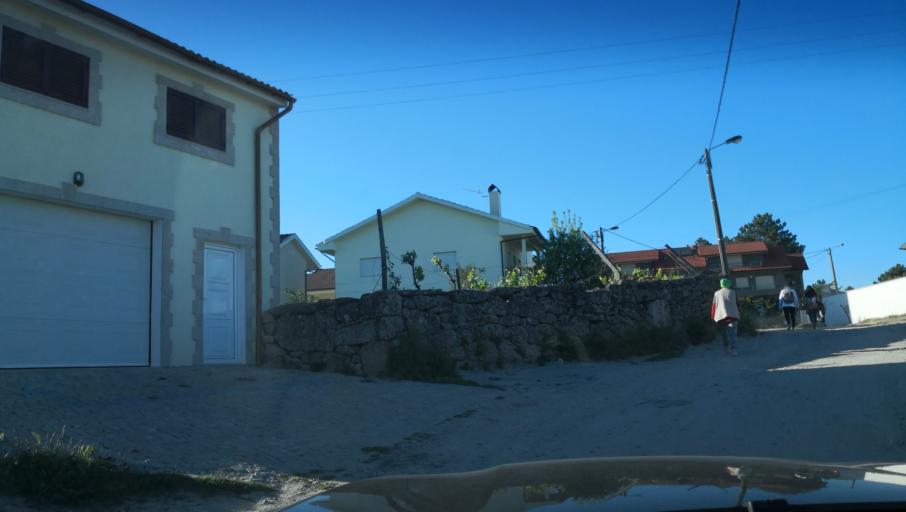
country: PT
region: Vila Real
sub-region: Vila Real
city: Vila Real
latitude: 41.3286
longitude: -7.6920
